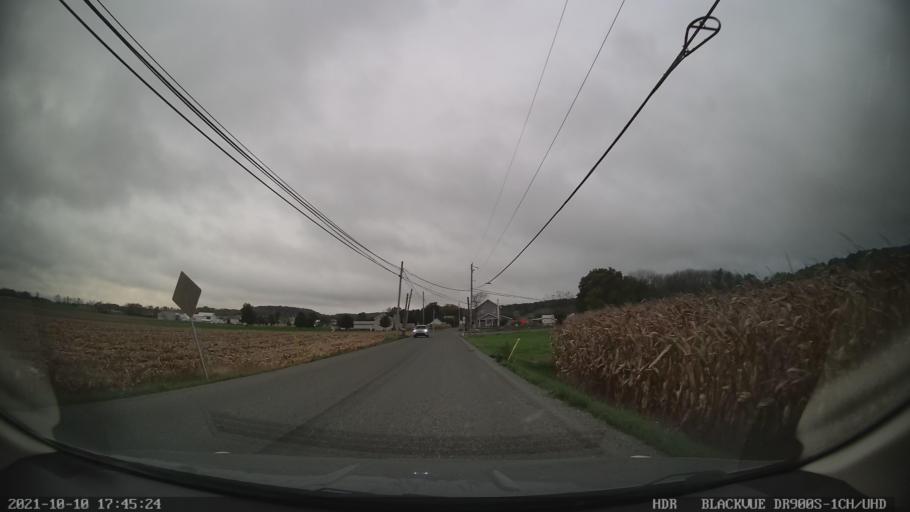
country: US
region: Pennsylvania
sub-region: Lehigh County
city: Breinigsville
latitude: 40.5516
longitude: -75.6766
